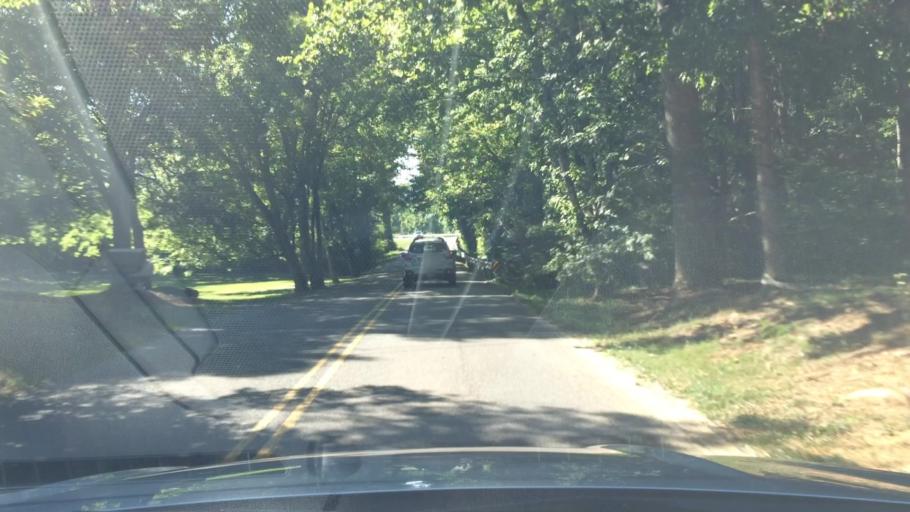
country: US
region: Tennessee
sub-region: Loudon County
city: Greenback
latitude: 35.7565
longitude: -84.1332
